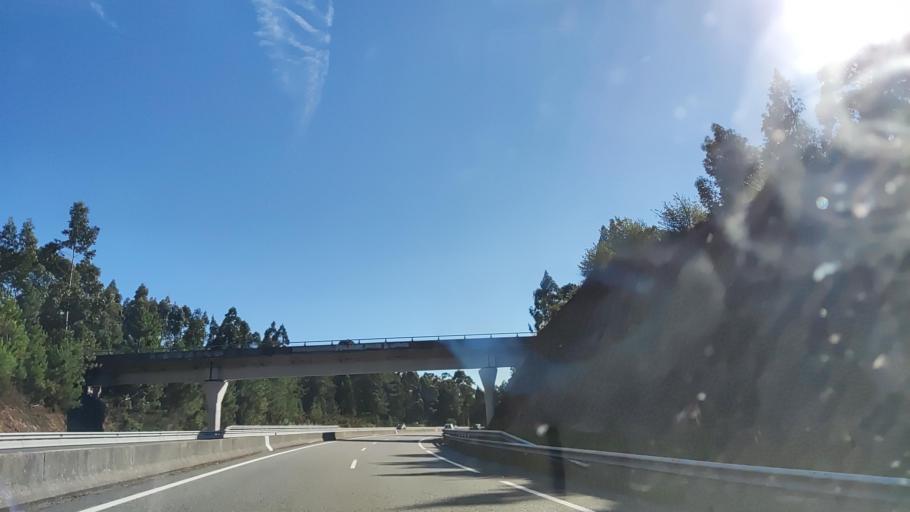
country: ES
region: Galicia
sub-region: Provincia da Coruna
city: Boiro
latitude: 42.5909
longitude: -8.9693
